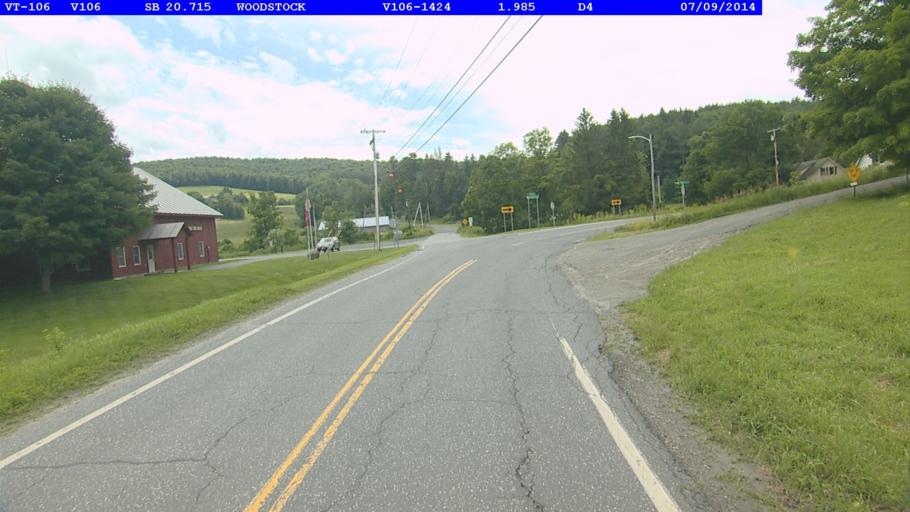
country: US
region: Vermont
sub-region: Windsor County
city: Woodstock
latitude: 43.5587
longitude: -72.5329
